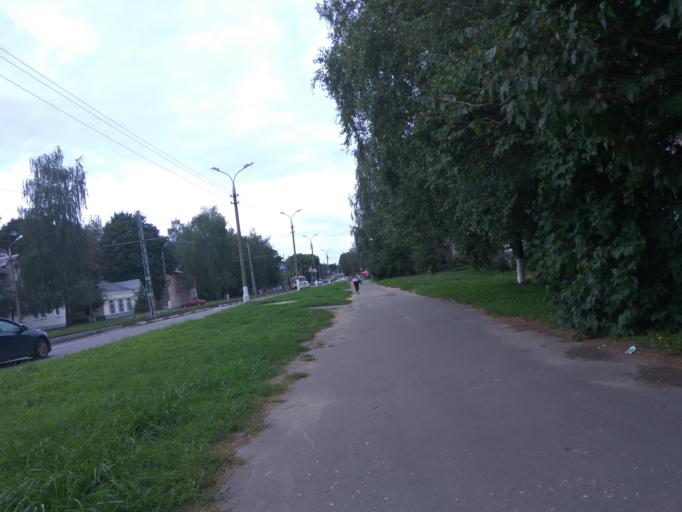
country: RU
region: Moskovskaya
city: Kolomna
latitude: 55.0782
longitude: 38.7720
